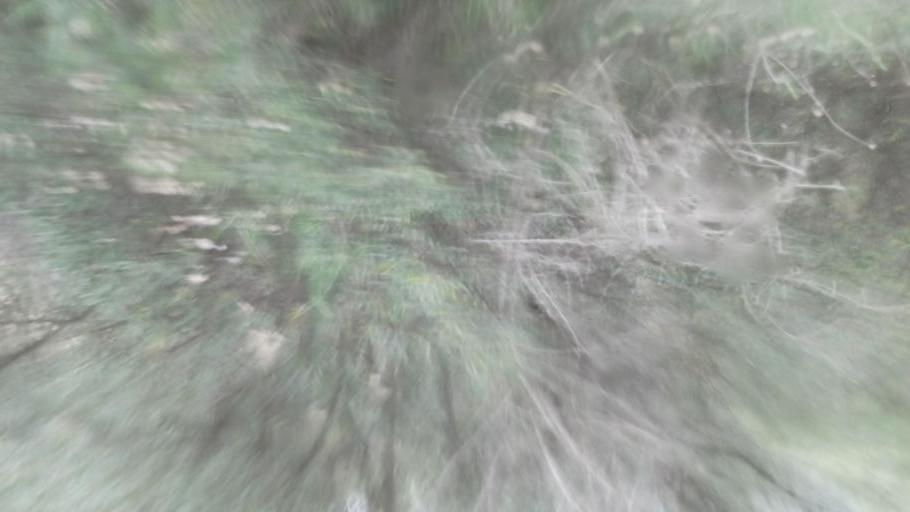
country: CY
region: Limassol
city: Parekklisha
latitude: 34.8574
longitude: 33.1073
